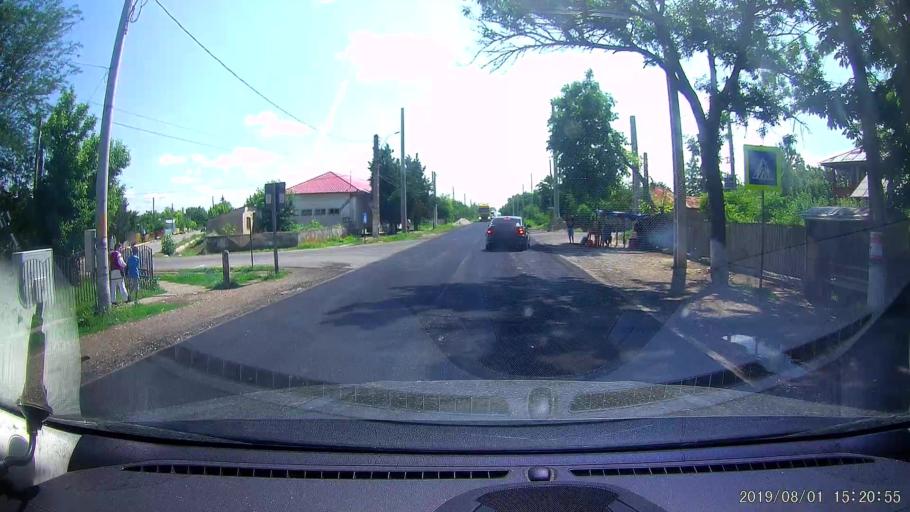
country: RO
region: Braila
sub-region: Comuna Tufesti
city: Tufesti
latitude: 45.0750
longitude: 27.8022
